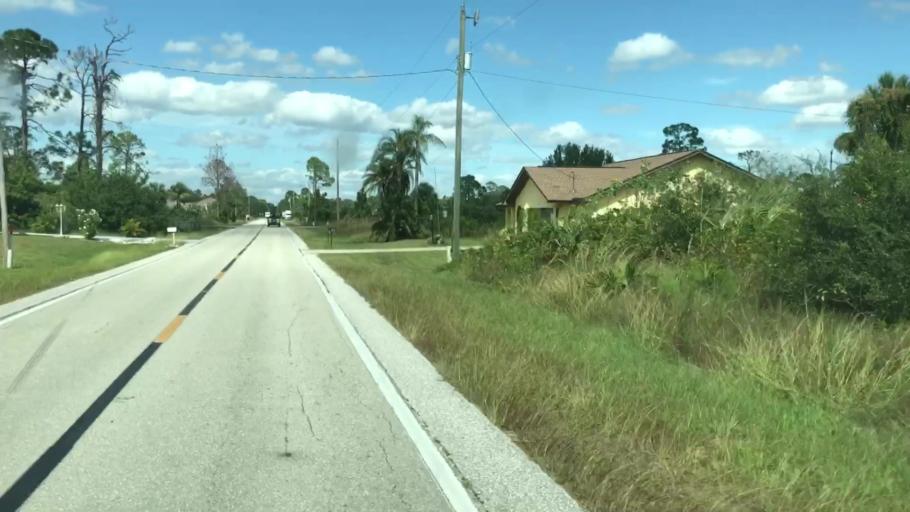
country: US
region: Florida
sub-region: Lee County
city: Lehigh Acres
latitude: 26.6310
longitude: -81.6252
